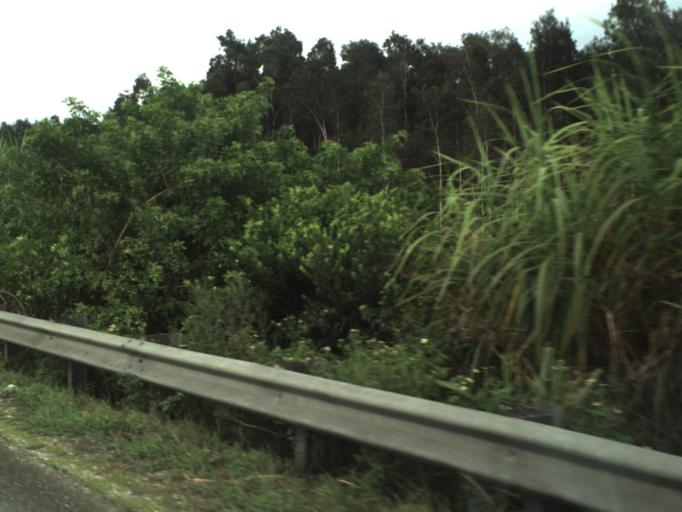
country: US
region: Florida
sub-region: Miami-Dade County
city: Kendall West
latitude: 25.7107
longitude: -80.4794
